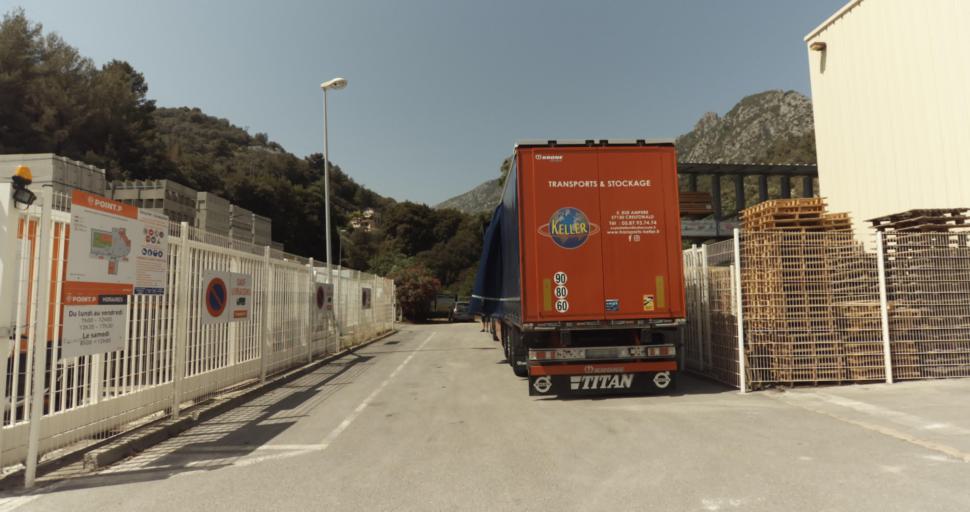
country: FR
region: Provence-Alpes-Cote d'Azur
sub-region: Departement des Alpes-Maritimes
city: Sainte-Agnes
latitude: 43.8083
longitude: 7.4871
